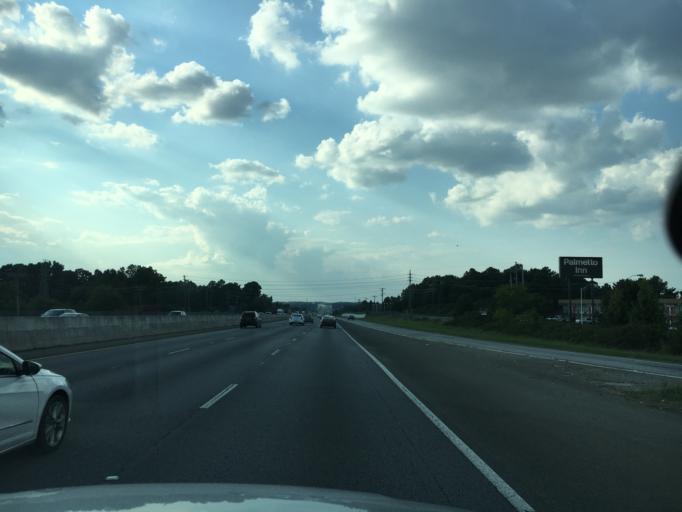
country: US
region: South Carolina
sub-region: Greenville County
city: Simpsonville
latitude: 34.7215
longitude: -82.2572
